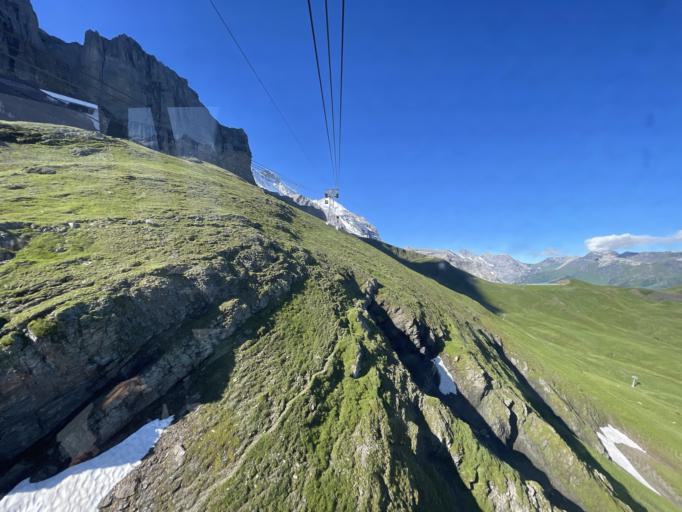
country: CH
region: Bern
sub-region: Interlaken-Oberhasli District
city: Grindelwald
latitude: 46.5834
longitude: 7.9828
